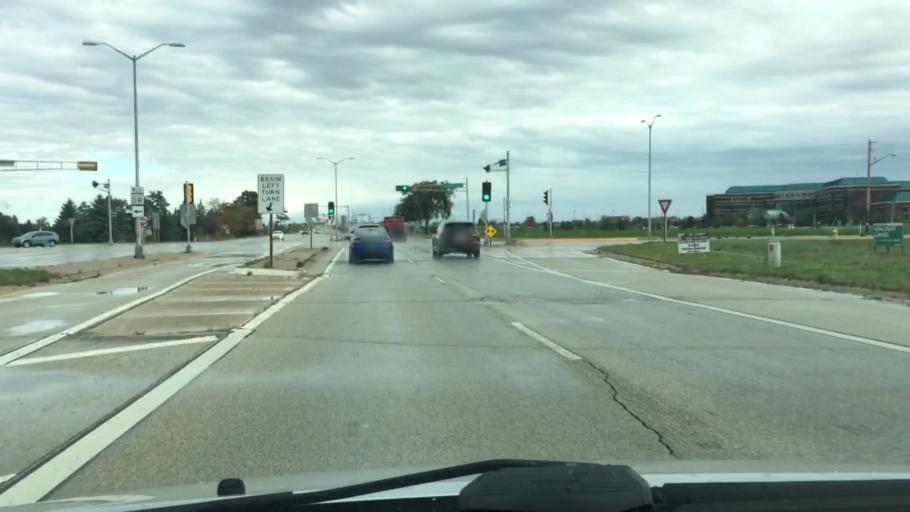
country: US
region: Wisconsin
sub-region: Waukesha County
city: Dousman
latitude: 43.0614
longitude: -88.4715
